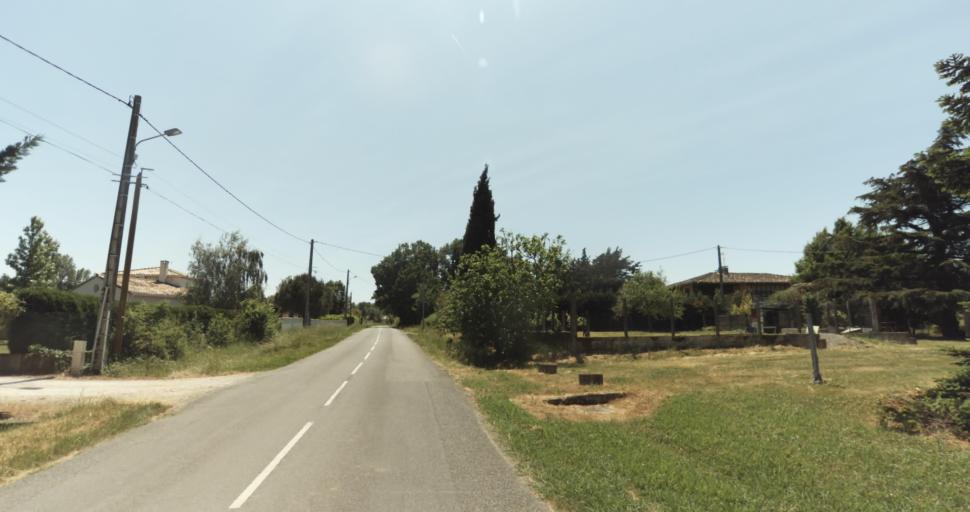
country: FR
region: Midi-Pyrenees
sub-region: Departement de la Haute-Garonne
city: Levignac
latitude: 43.6437
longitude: 1.1748
